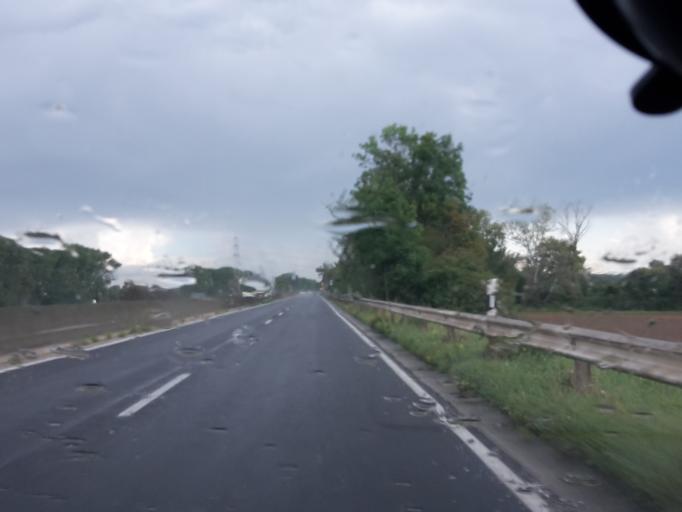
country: DE
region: Hesse
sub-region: Regierungsbezirk Darmstadt
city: Ginsheim-Gustavsburg
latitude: 49.9605
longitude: 8.3293
